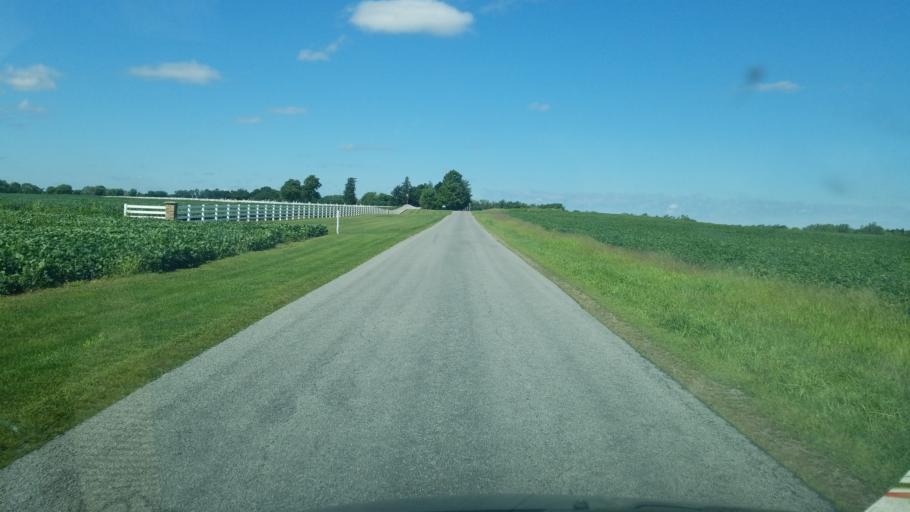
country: US
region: Ohio
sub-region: Wood County
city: North Baltimore
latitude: 41.1242
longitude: -83.6985
